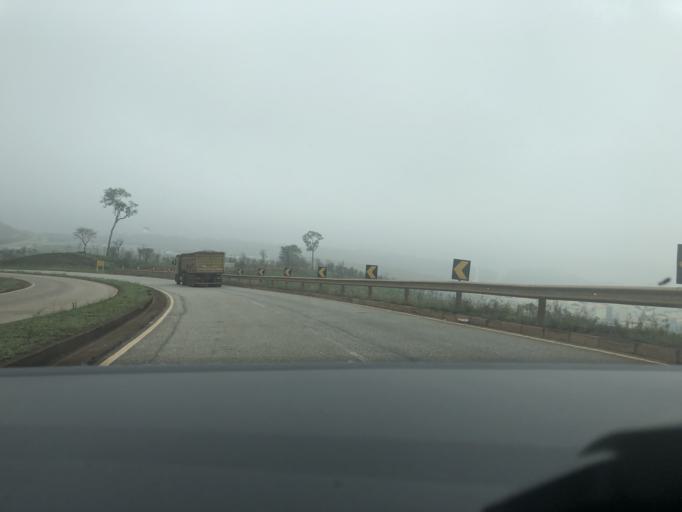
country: BR
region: Minas Gerais
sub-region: Congonhas
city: Congonhas
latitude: -20.5918
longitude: -43.9530
